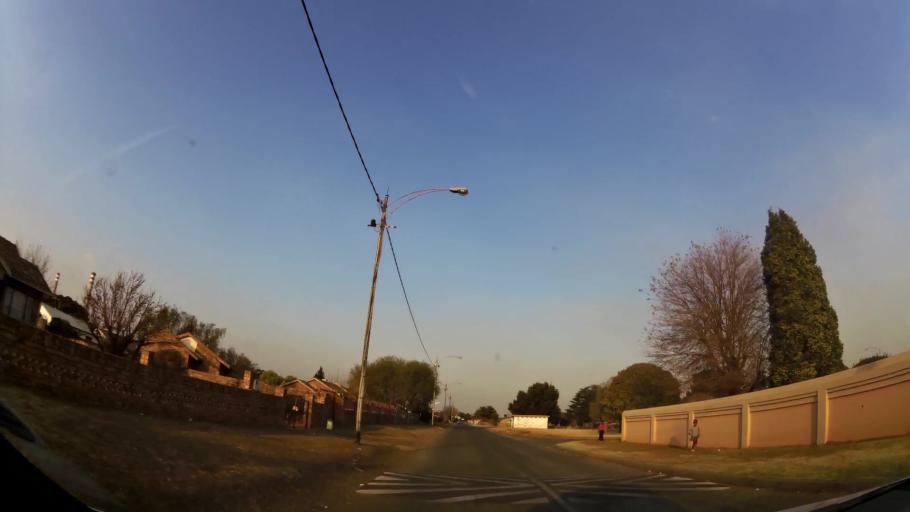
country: ZA
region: Gauteng
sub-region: Ekurhuleni Metropolitan Municipality
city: Springs
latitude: -26.2638
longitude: 28.4060
